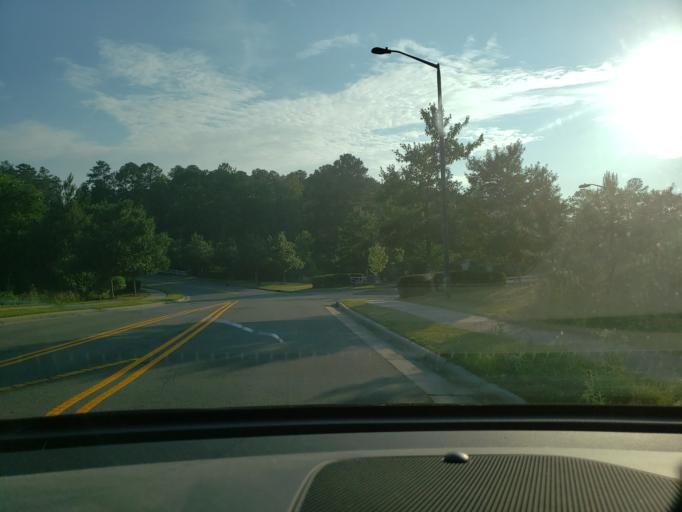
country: US
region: North Carolina
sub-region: Durham County
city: Durham
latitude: 35.9423
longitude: -78.9107
